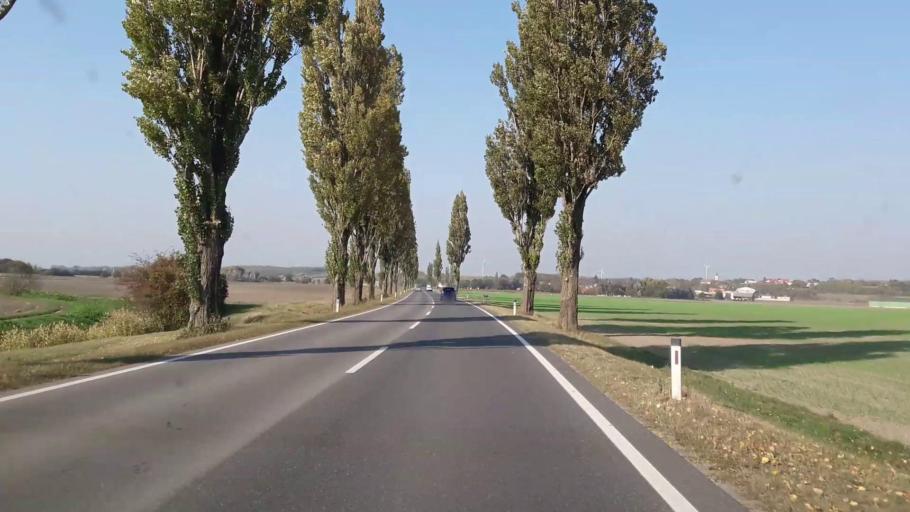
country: AT
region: Lower Austria
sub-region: Politischer Bezirk Ganserndorf
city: Engelhartstetten
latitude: 48.2097
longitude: 16.9026
